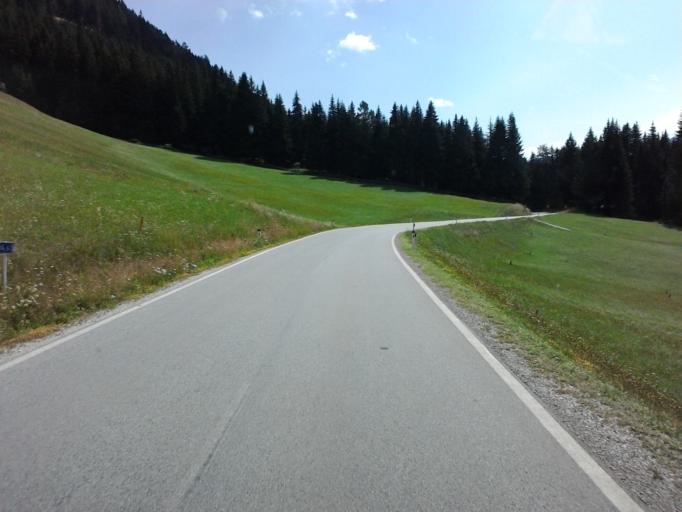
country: AT
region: Tyrol
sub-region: Politischer Bezirk Lienz
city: Obertilliach
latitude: 46.7145
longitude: 12.5729
